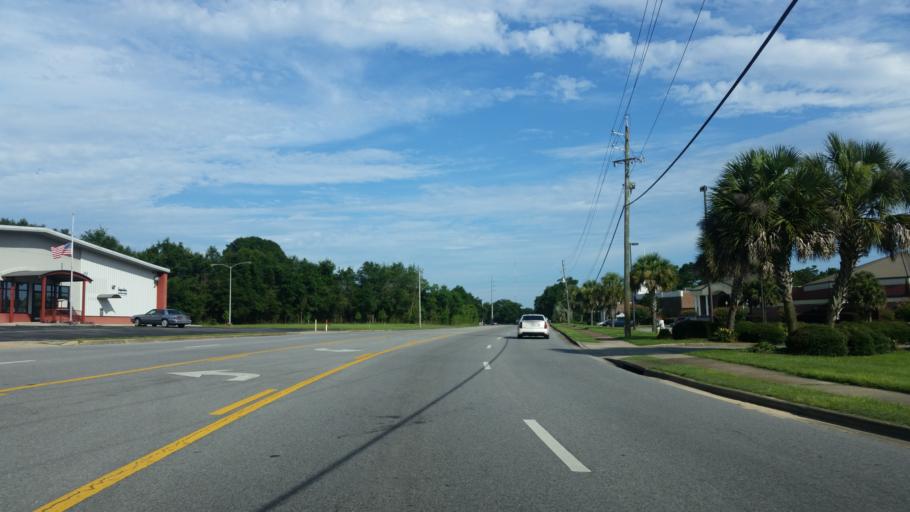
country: US
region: Florida
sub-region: Escambia County
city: Goulding
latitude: 30.4409
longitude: -87.2275
